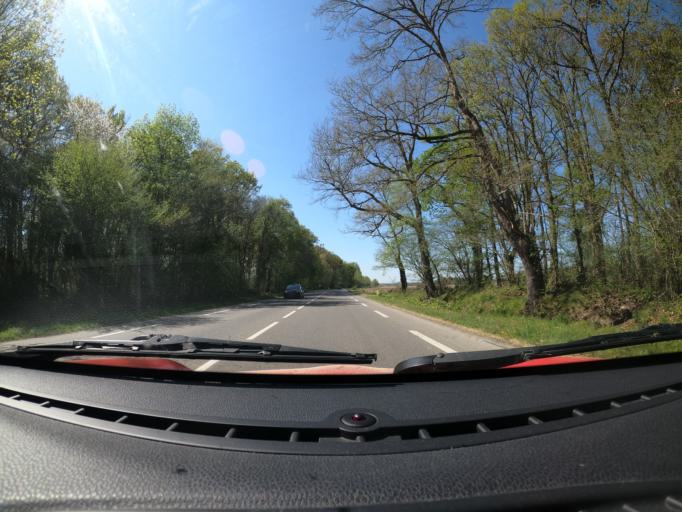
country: FR
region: Aquitaine
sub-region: Departement des Pyrenees-Atlantiques
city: Lescar
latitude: 43.3403
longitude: -0.4039
